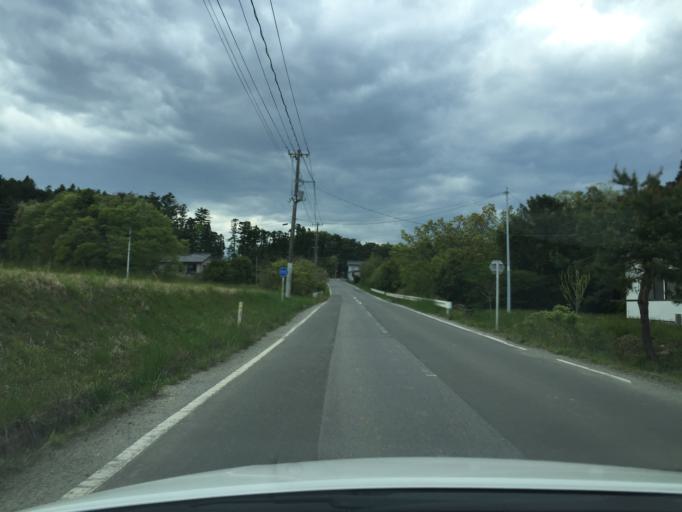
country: JP
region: Fukushima
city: Namie
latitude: 37.7441
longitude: 141.0033
